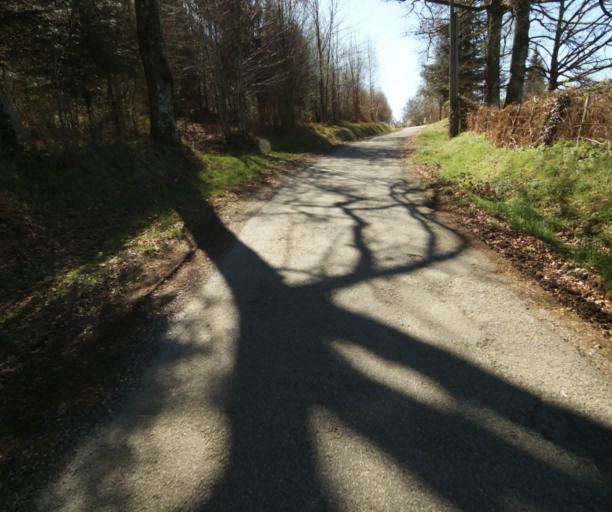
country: FR
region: Limousin
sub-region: Departement de la Correze
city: Seilhac
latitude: 45.3610
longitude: 1.7198
